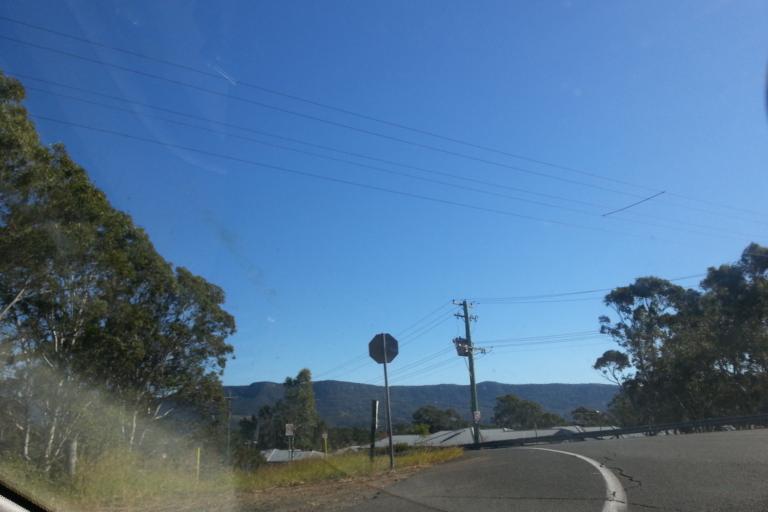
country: AU
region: New South Wales
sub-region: Wollongong
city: Dapto
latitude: -34.5171
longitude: 150.7834
